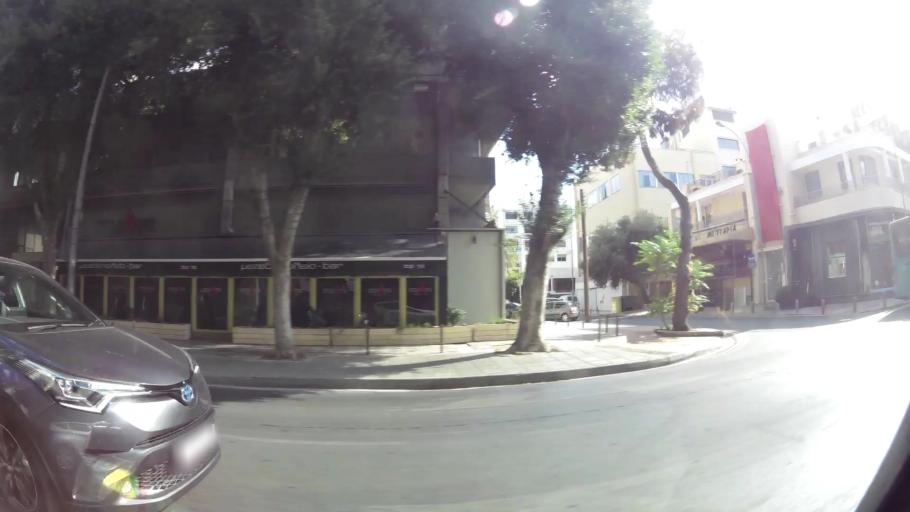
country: CY
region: Lefkosia
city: Nicosia
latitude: 35.1684
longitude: 33.3583
